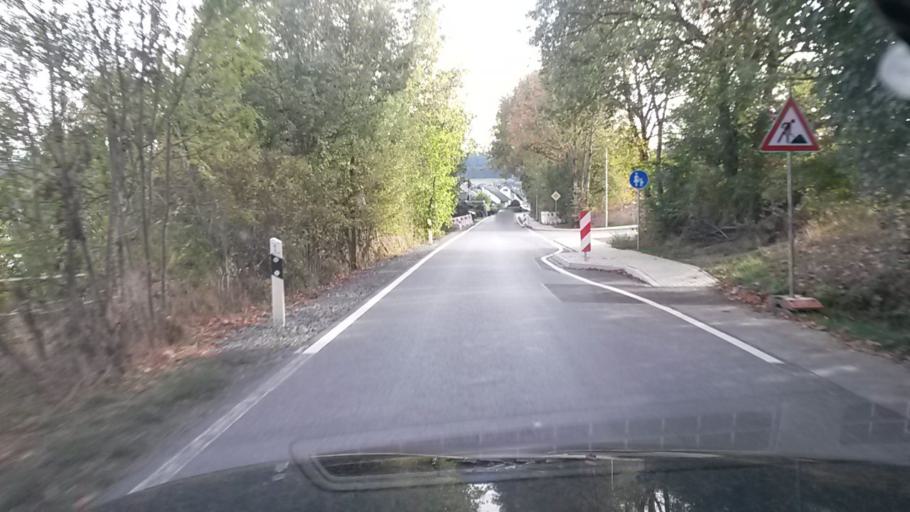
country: DE
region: North Rhine-Westphalia
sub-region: Regierungsbezirk Arnsberg
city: Herscheid
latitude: 51.1848
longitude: 7.7495
